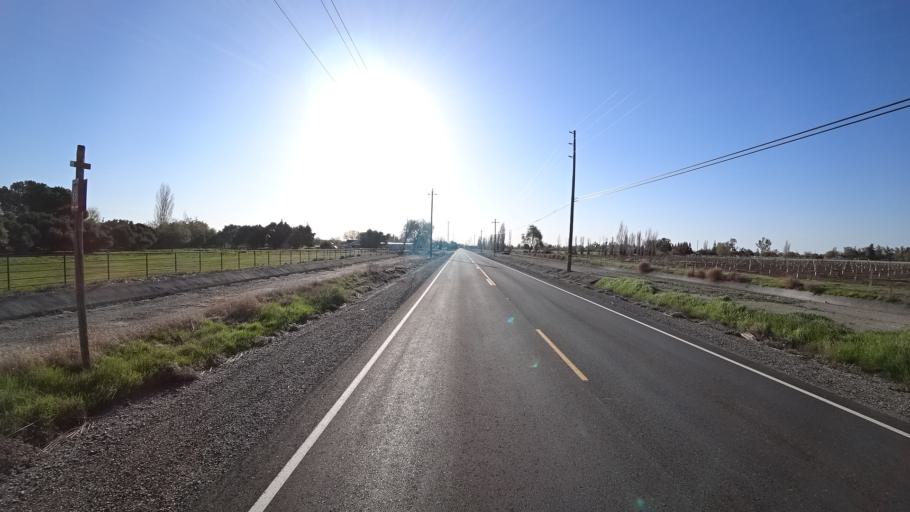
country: US
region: California
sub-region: Glenn County
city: Orland
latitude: 39.7643
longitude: -122.2406
